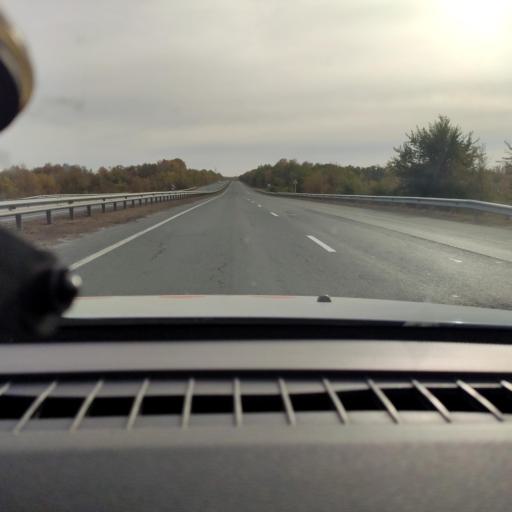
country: RU
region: Samara
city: Novokuybyshevsk
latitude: 53.0398
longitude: 50.0022
